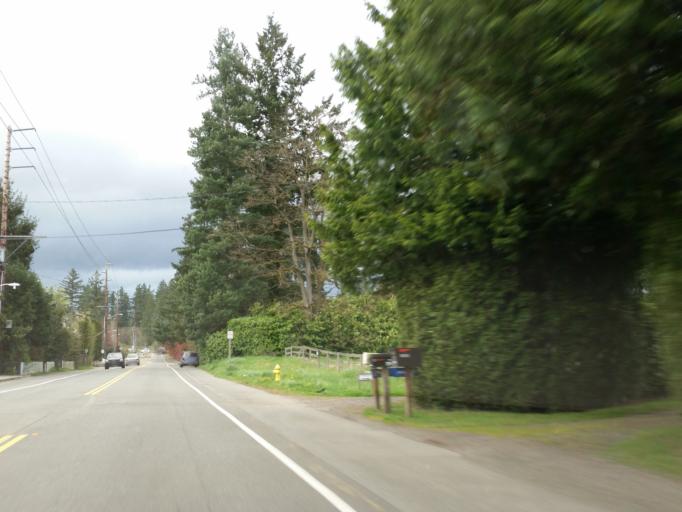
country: US
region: Washington
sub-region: King County
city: Woodinville
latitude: 47.7731
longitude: -122.1667
